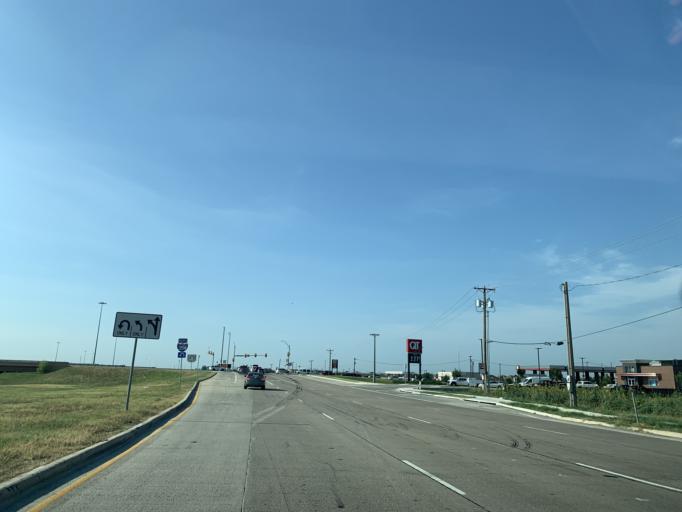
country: US
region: Texas
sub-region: Tarrant County
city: Blue Mound
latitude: 32.8745
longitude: -97.3182
